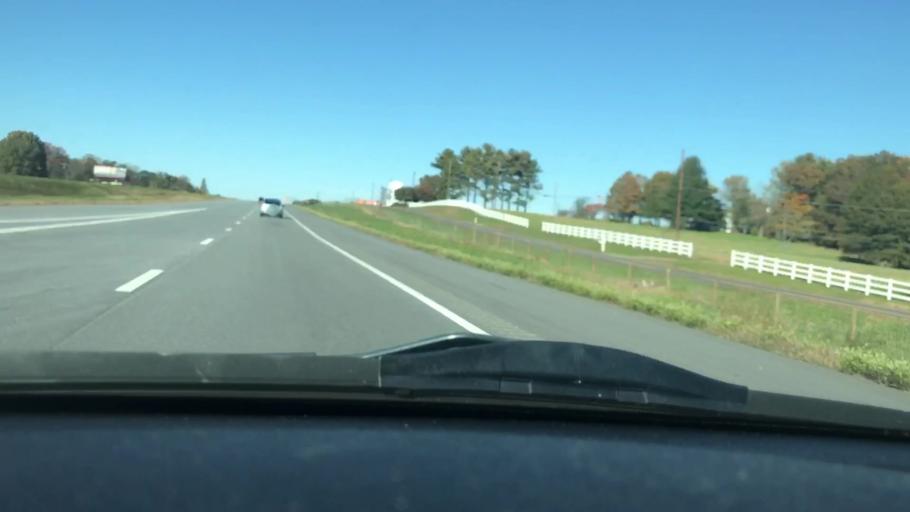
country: US
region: North Carolina
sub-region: Guilford County
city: Stokesdale
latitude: 36.2867
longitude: -79.9396
